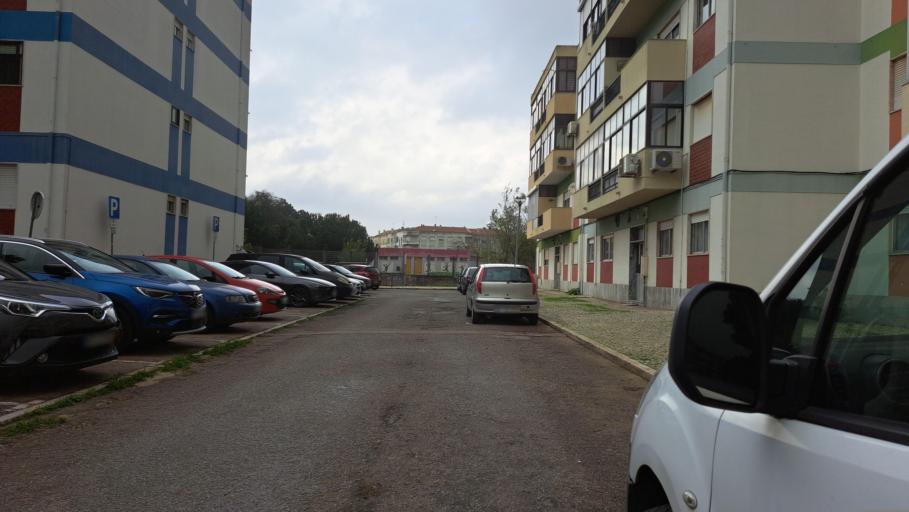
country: PT
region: Setubal
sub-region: Moita
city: Alhos Vedros
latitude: 38.6490
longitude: -9.0435
